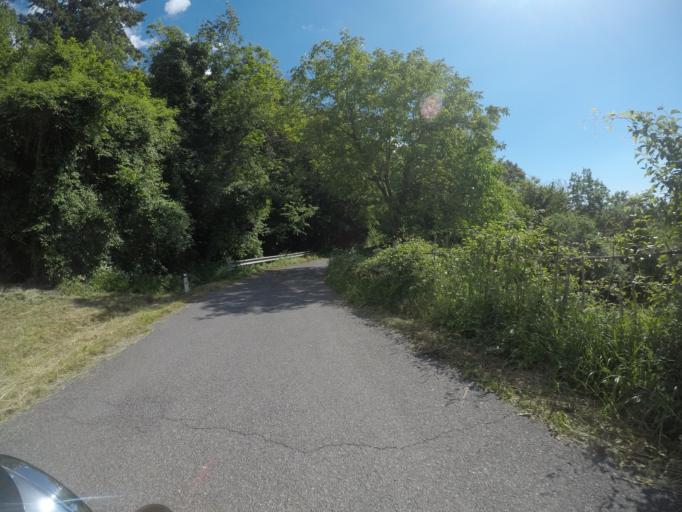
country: IT
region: Tuscany
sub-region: Provincia di Massa-Carrara
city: Casola in Lunigiana
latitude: 44.1773
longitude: 10.1521
